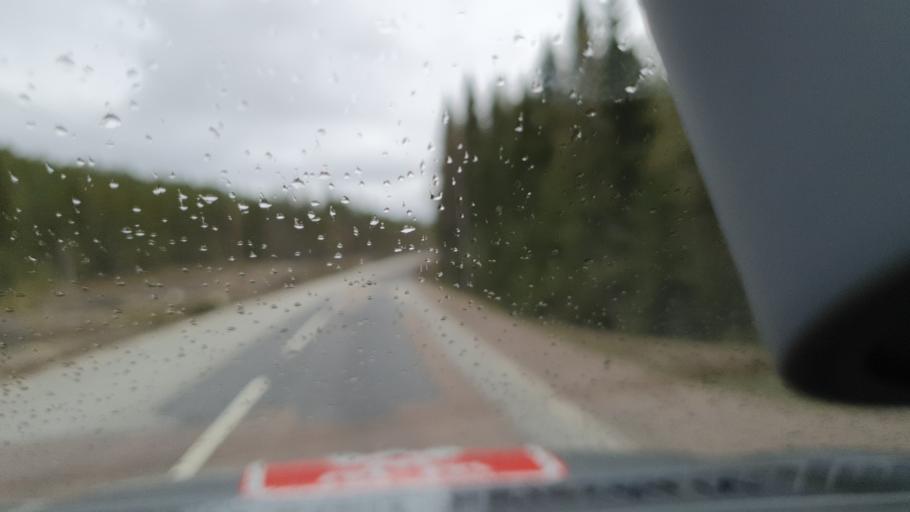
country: SE
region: Vaesternorrland
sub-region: Solleftea Kommun
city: Solleftea
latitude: 63.6311
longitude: 17.4384
